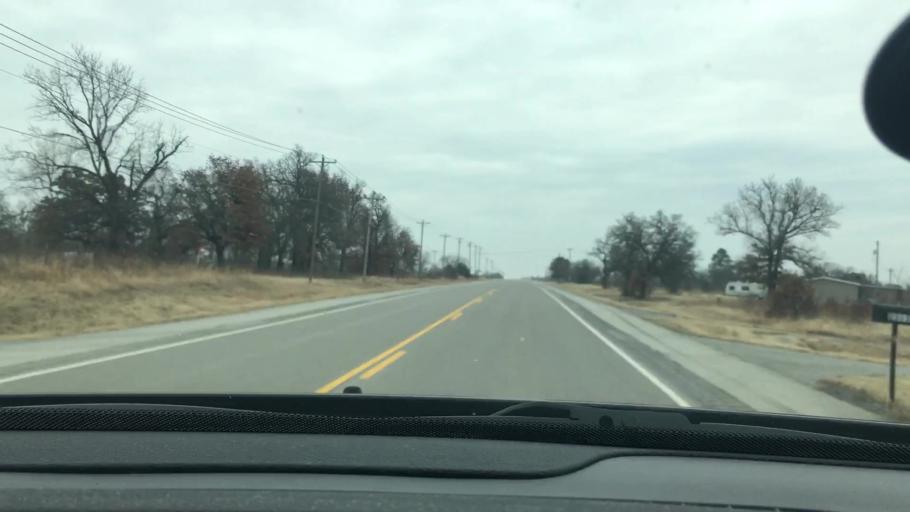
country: US
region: Oklahoma
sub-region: Carter County
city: Healdton
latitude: 34.4008
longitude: -97.5063
